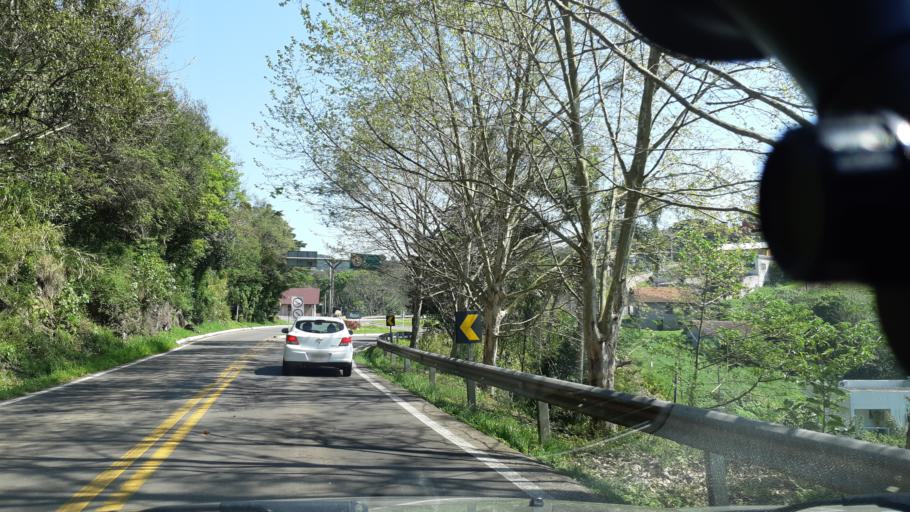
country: BR
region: Rio Grande do Sul
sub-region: Nova Petropolis
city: Nova Petropolis
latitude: -29.3928
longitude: -51.1237
